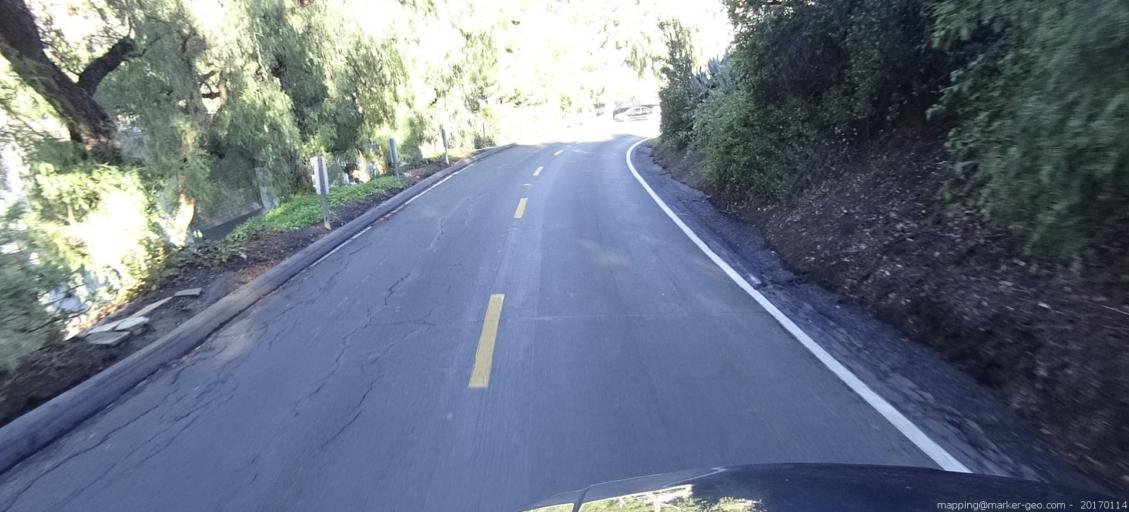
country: US
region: California
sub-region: Orange County
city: North Tustin
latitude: 33.7774
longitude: -117.7969
